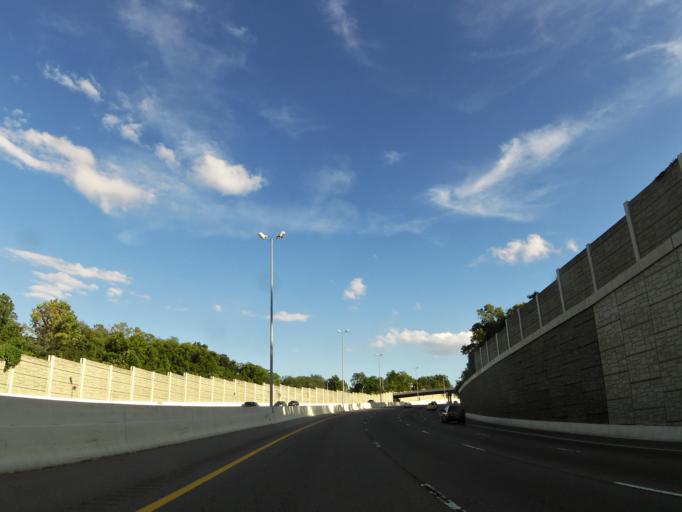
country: US
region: Tennessee
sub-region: Davidson County
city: Lakewood
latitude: 36.1739
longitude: -86.6897
